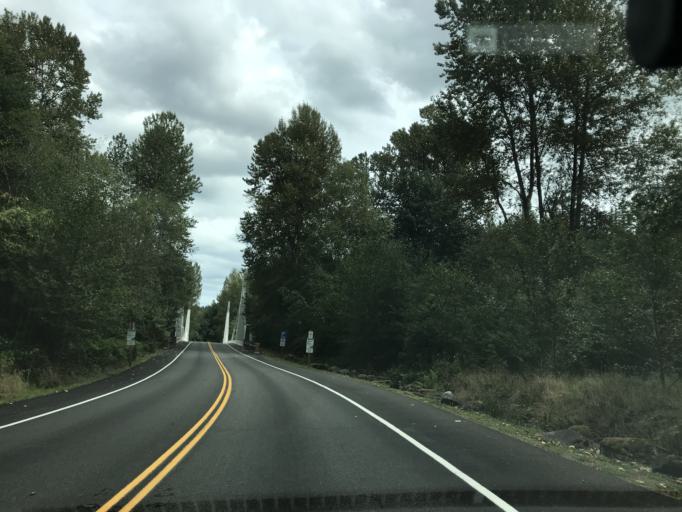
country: US
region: Washington
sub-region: King County
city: Black Diamond
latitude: 47.2792
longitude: -122.0409
